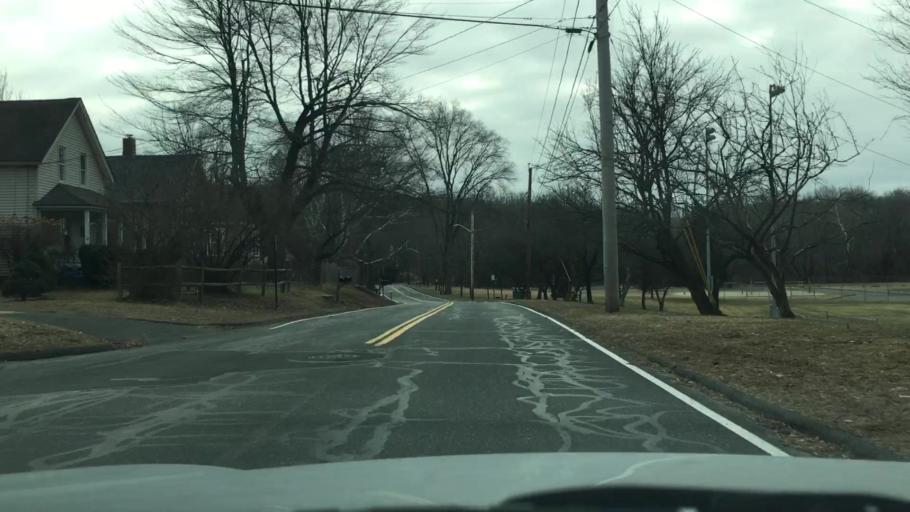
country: US
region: Massachusetts
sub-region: Hampshire County
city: Northampton
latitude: 42.3288
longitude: -72.6707
